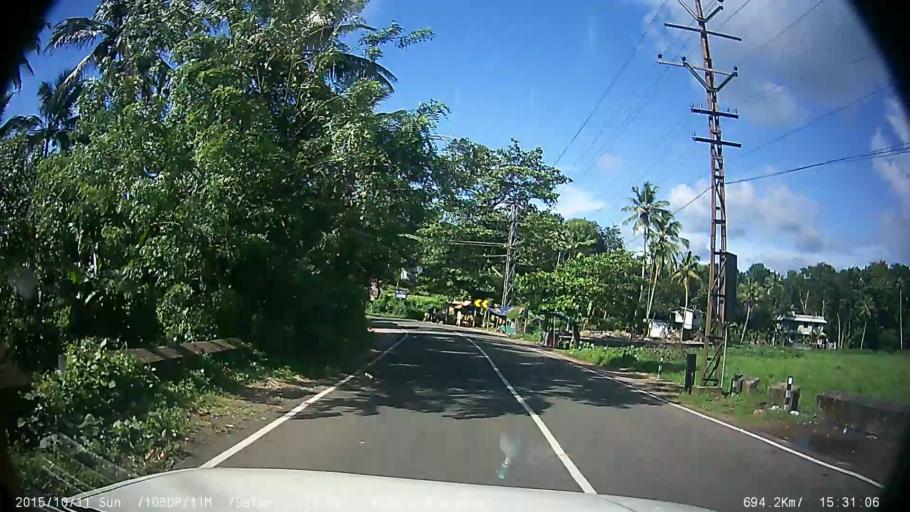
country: IN
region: Kerala
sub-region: Kottayam
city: Changanacheri
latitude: 9.5083
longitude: 76.5717
